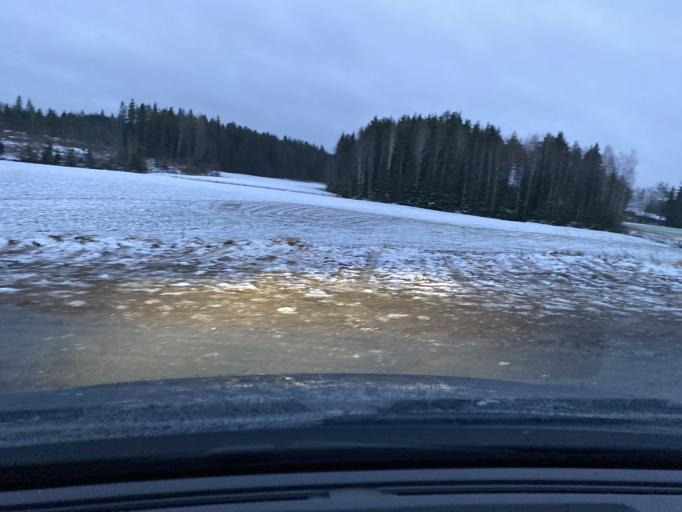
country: FI
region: Pirkanmaa
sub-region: Lounais-Pirkanmaa
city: Punkalaidun
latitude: 61.1641
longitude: 22.9641
